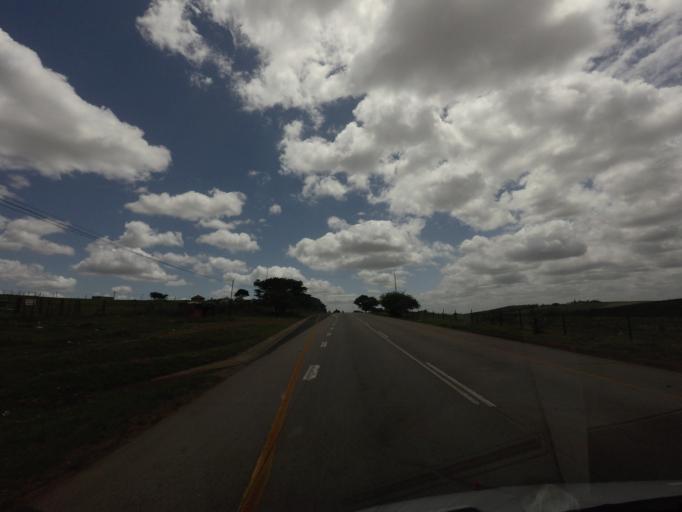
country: ZA
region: KwaZulu-Natal
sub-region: uMkhanyakude District Municipality
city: Mtubatuba
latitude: -28.4782
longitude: 32.1441
